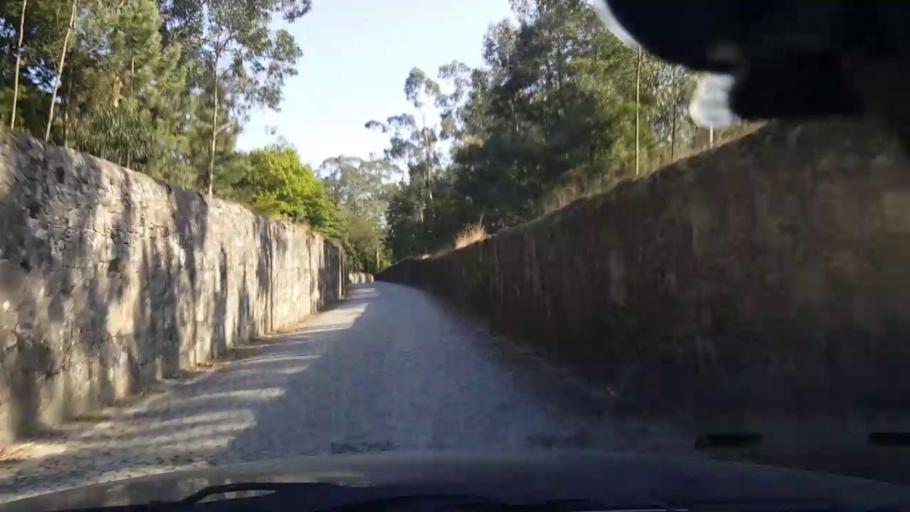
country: PT
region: Porto
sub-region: Vila do Conde
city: Arvore
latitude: 41.3445
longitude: -8.6890
